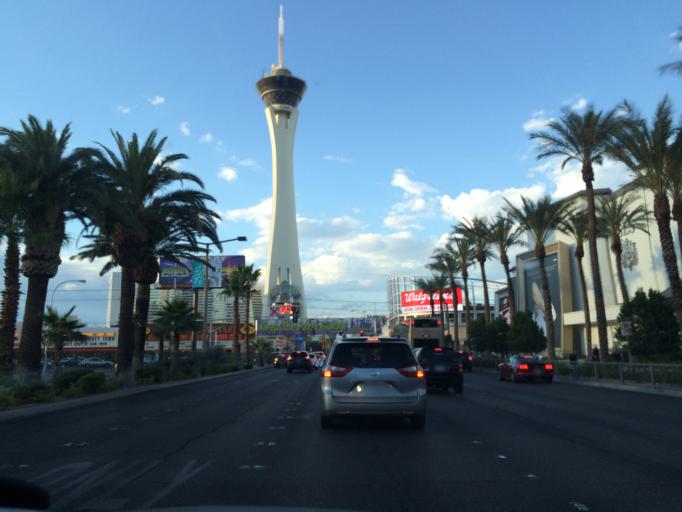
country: US
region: Nevada
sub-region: Clark County
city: Las Vegas
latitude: 36.1427
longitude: -115.1579
